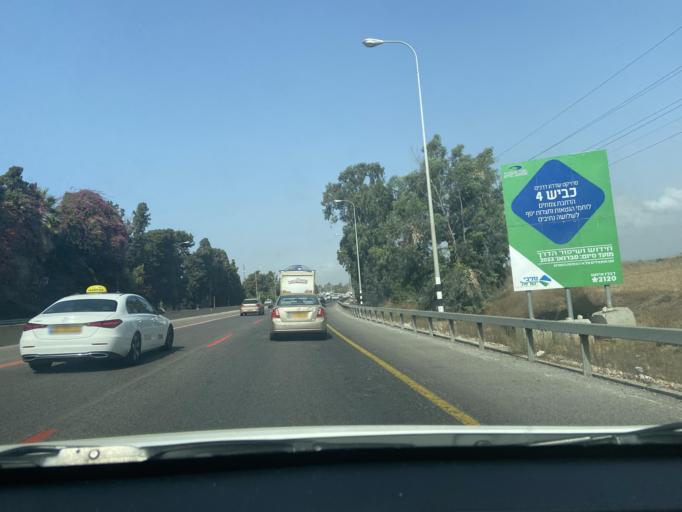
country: IL
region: Northern District
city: `Akko
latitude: 32.9542
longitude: 35.0910
